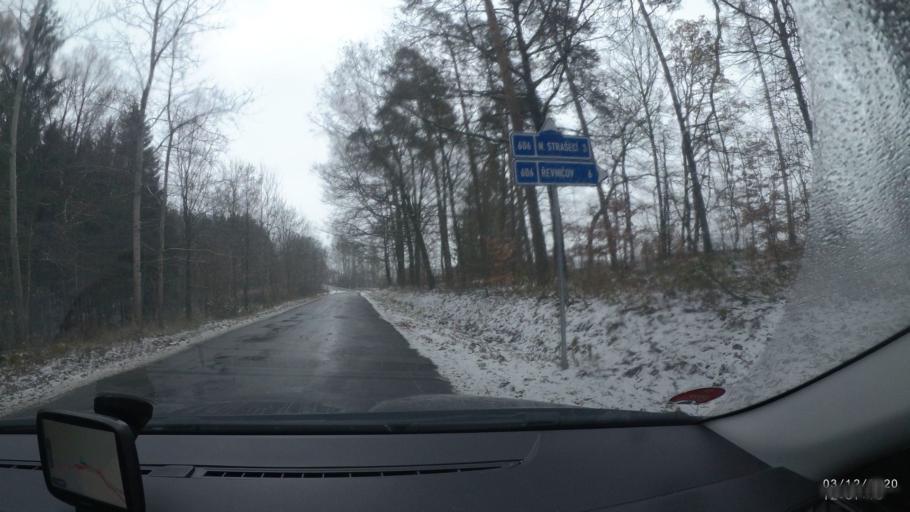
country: CZ
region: Central Bohemia
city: Nove Straseci
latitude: 50.1665
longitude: 13.8723
